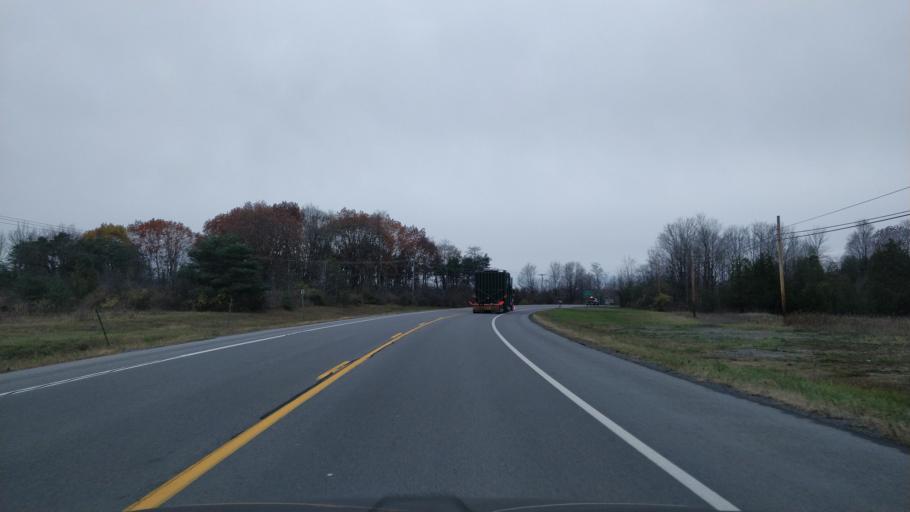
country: CA
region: Ontario
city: Brockville
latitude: 44.6149
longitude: -75.5982
